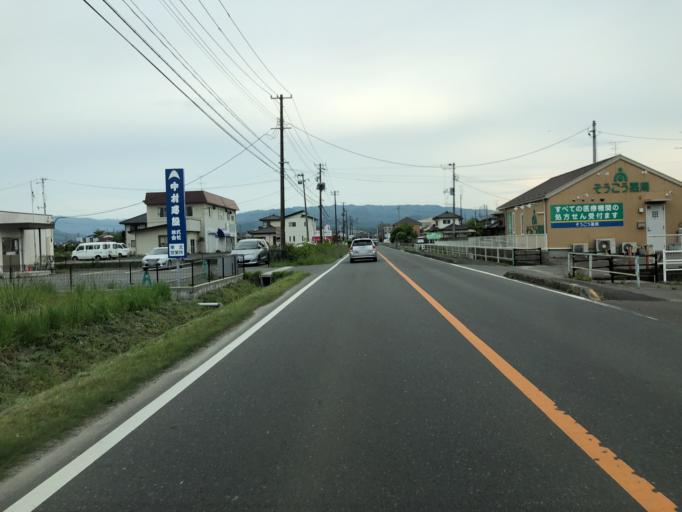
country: JP
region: Miyagi
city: Marumori
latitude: 37.7926
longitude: 140.9336
